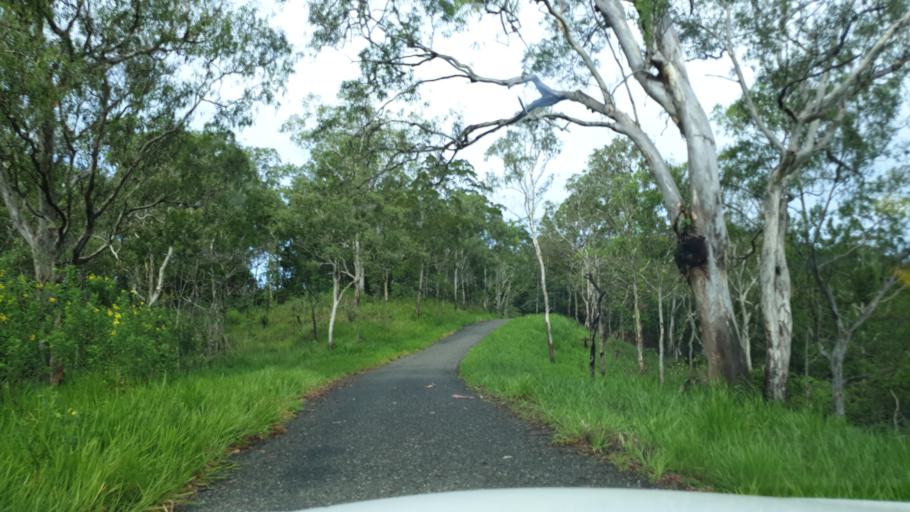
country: PG
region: National Capital
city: Port Moresby
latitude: -9.4350
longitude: 147.3751
